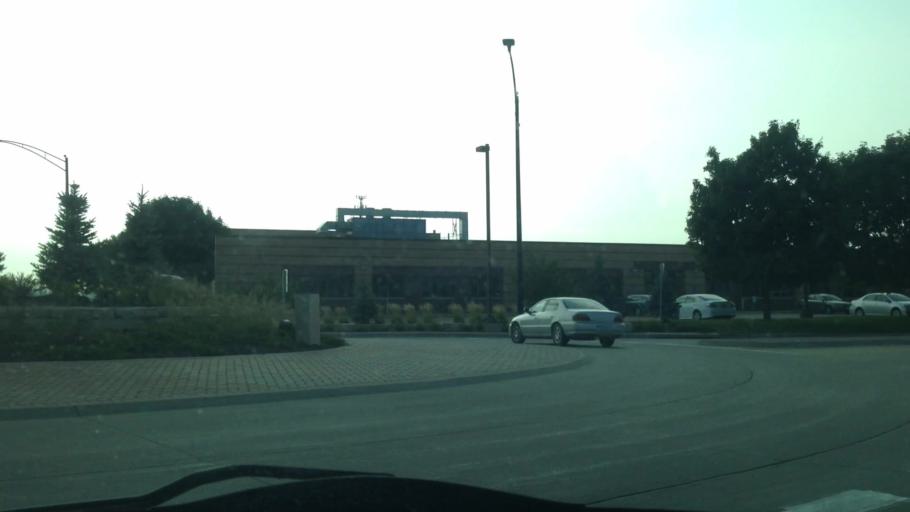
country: US
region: Iowa
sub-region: Johnson County
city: Coralville
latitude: 41.6957
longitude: -91.6136
